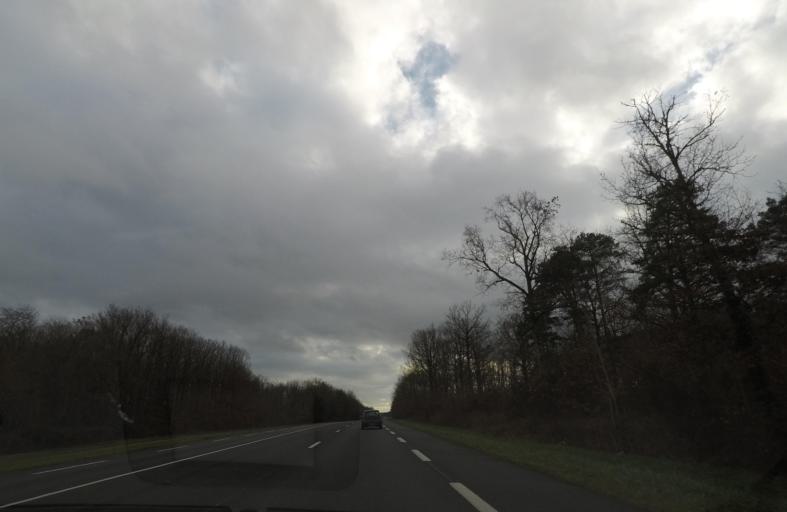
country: FR
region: Centre
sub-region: Departement du Loir-et-Cher
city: Soings-en-Sologne
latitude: 47.4545
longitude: 1.5294
